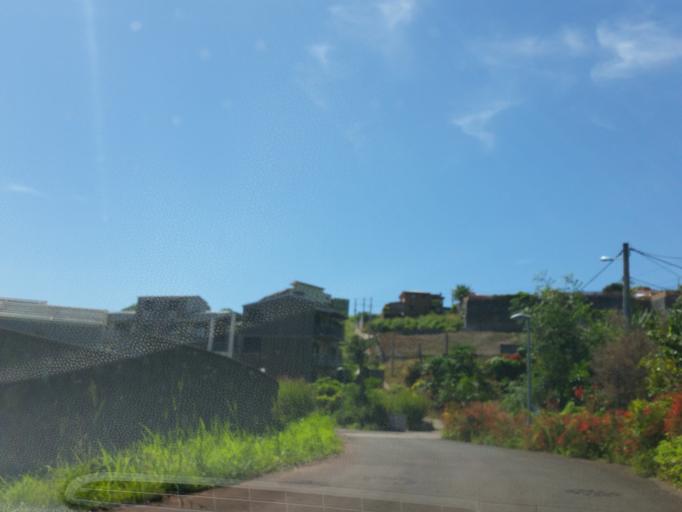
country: RE
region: Reunion
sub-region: Reunion
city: Sainte-Marie
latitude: -20.9180
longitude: 55.5226
